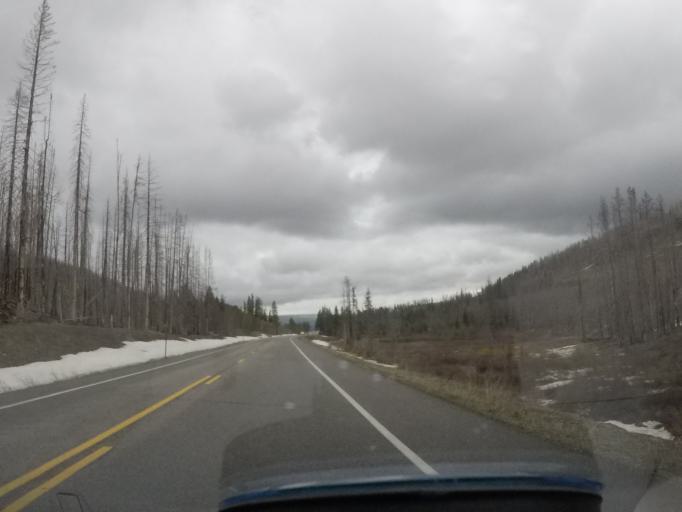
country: US
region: Idaho
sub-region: Teton County
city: Driggs
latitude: 44.0486
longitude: -110.6910
